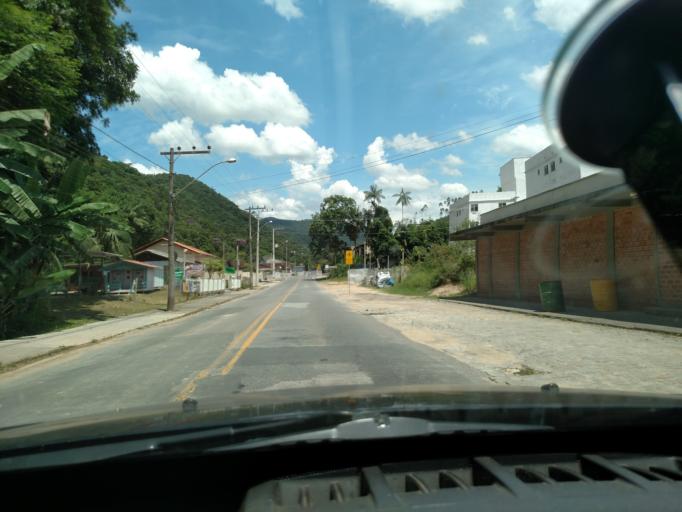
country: BR
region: Santa Catarina
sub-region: Blumenau
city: Blumenau
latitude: -26.9859
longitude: -49.0756
